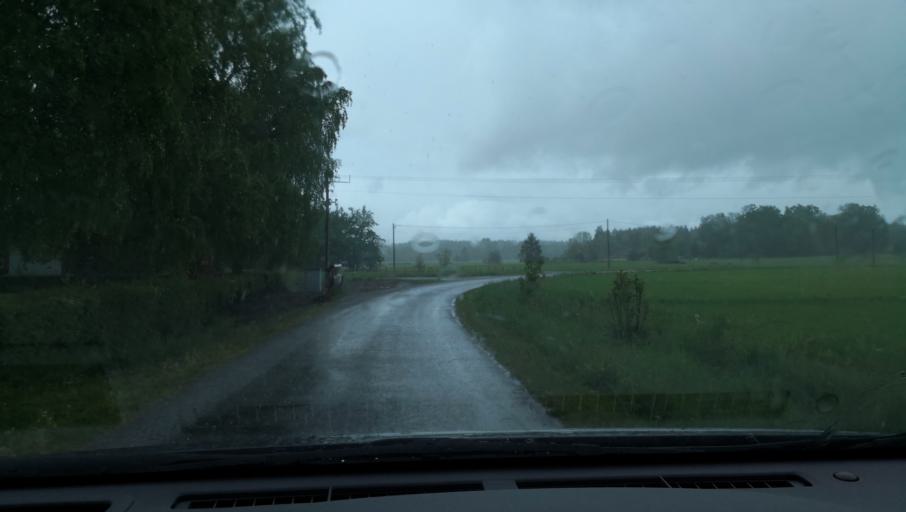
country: SE
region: Uppsala
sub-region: Enkopings Kommun
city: Orsundsbro
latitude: 59.7797
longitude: 17.3502
